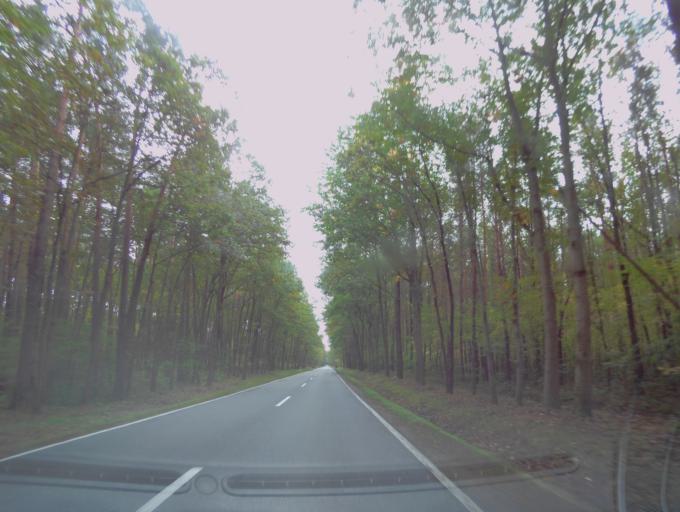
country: PL
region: Subcarpathian Voivodeship
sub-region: Powiat nizanski
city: Krzeszow
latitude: 50.3935
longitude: 22.3008
